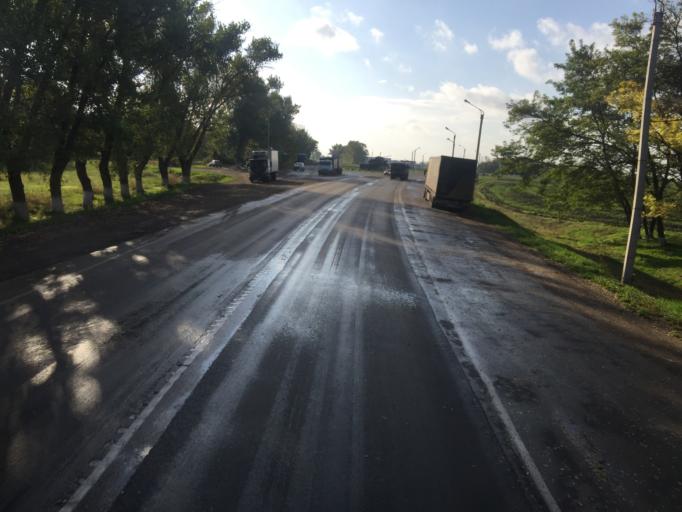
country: RU
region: Rostov
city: Yegorlykskaya
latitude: 46.5890
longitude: 40.6304
